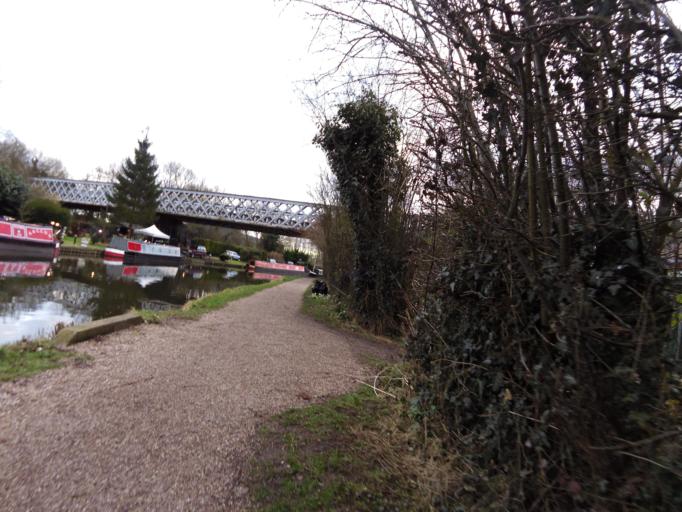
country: GB
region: England
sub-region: Hertfordshire
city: Watford
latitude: 51.6513
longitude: -0.4272
